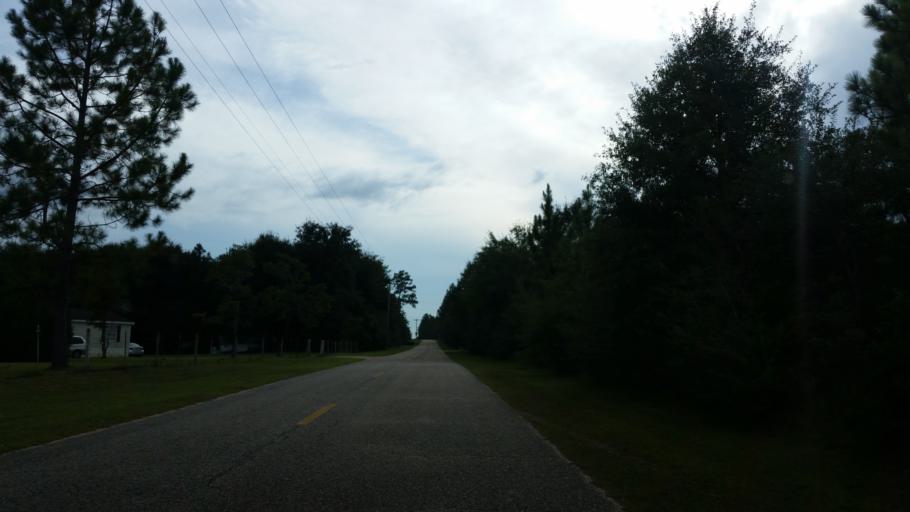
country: US
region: Florida
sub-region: Santa Rosa County
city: Point Baker
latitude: 30.7252
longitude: -86.9072
